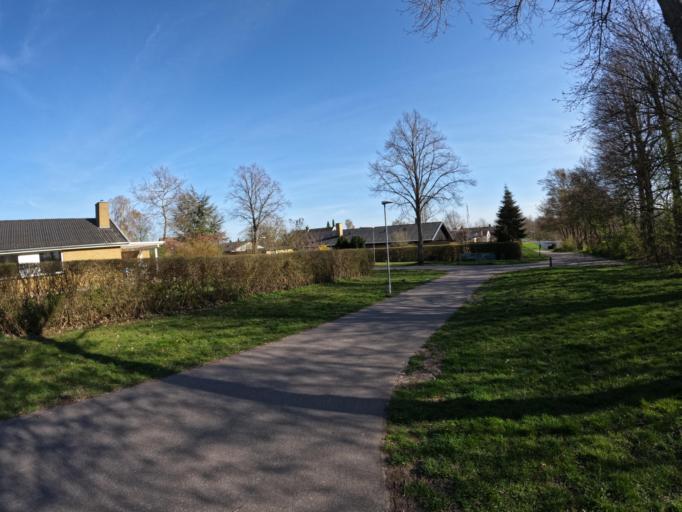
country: DK
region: Capital Region
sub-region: Hoje-Taastrup Kommune
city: Flong
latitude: 55.6482
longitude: 12.2209
